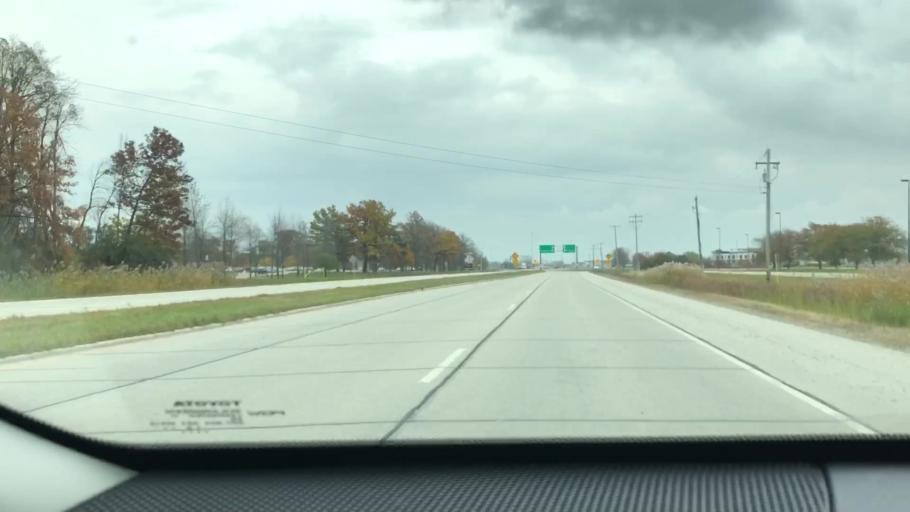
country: US
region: Wisconsin
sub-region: Brown County
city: Oneida
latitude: 44.4956
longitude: -88.1294
